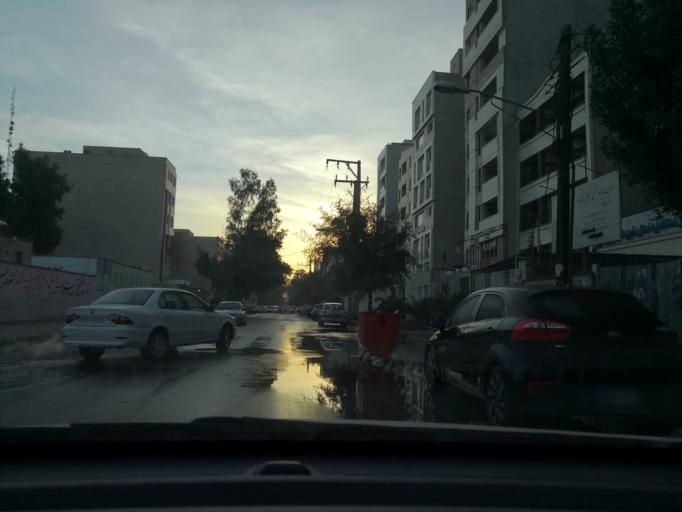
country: IR
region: Khuzestan
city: Ahvaz
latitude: 31.3517
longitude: 48.6814
